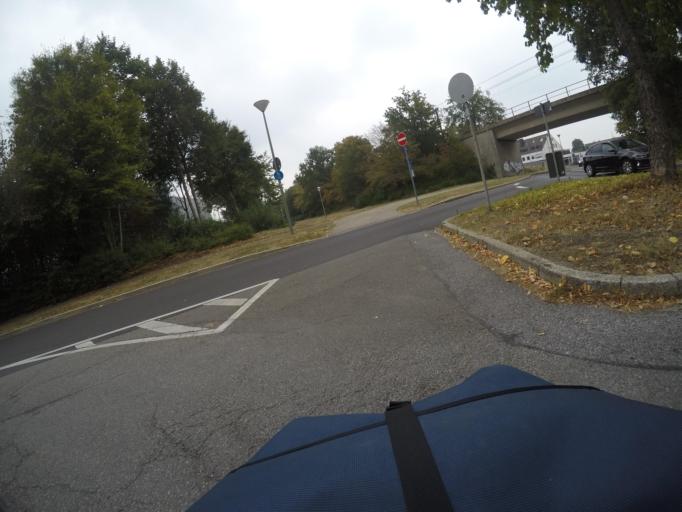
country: DE
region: North Rhine-Westphalia
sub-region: Regierungsbezirk Dusseldorf
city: Krefeld
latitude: 51.3204
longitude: 6.5852
